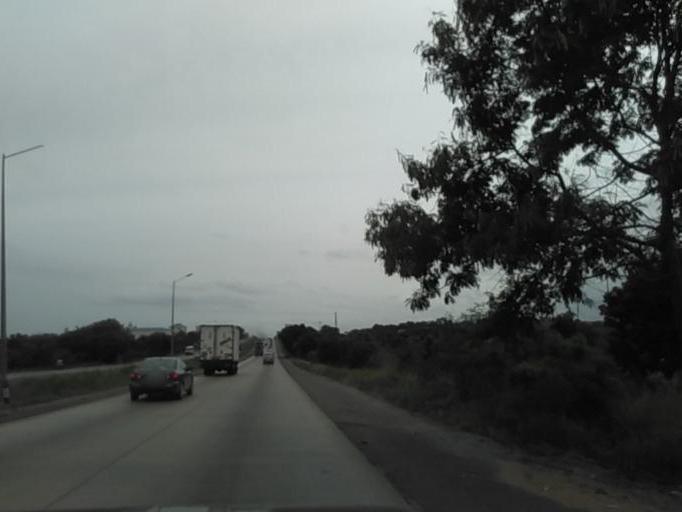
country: GH
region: Greater Accra
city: Medina Estates
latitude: 5.6286
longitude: -0.1597
